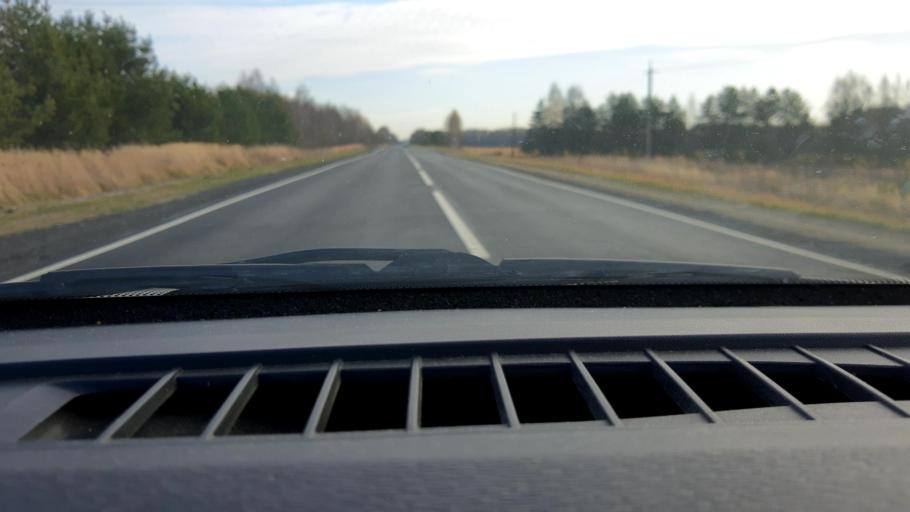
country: RU
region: Nizjnij Novgorod
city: Novaya Balakhna
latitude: 56.5953
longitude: 43.6482
